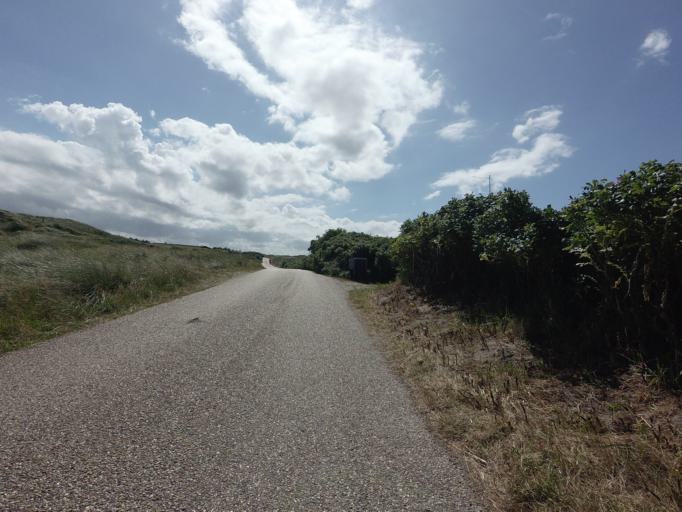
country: DK
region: North Denmark
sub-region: Jammerbugt Kommune
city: Pandrup
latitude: 57.3065
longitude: 9.6481
